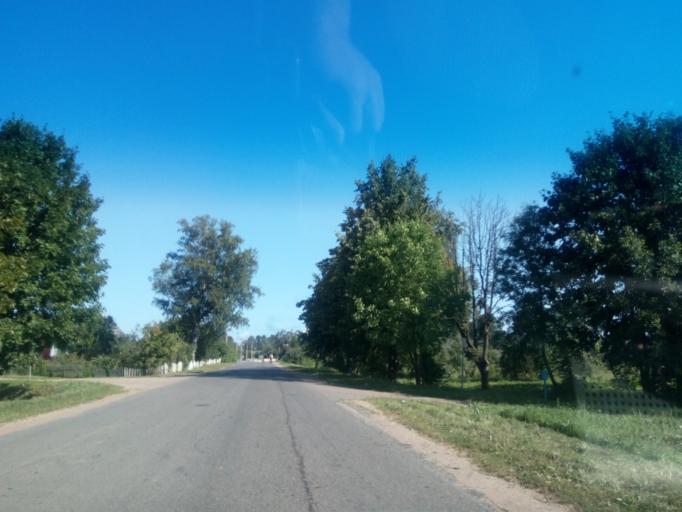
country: BY
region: Vitebsk
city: Dzisna
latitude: 55.6643
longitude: 28.3259
